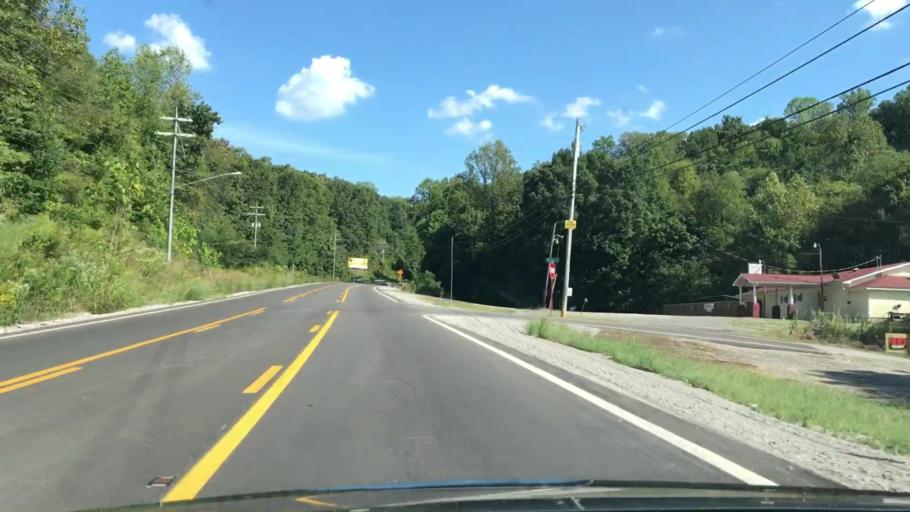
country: US
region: Alabama
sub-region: Limestone County
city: Ardmore
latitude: 35.0047
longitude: -86.8719
